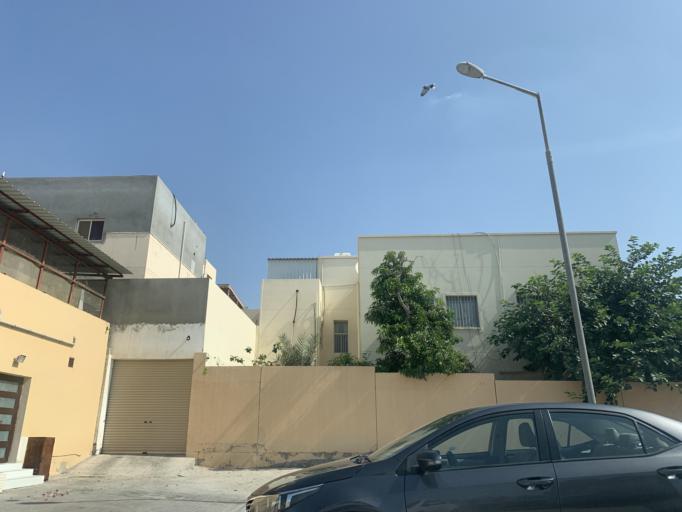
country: BH
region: Central Governorate
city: Madinat Hamad
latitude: 26.1281
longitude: 50.5005
